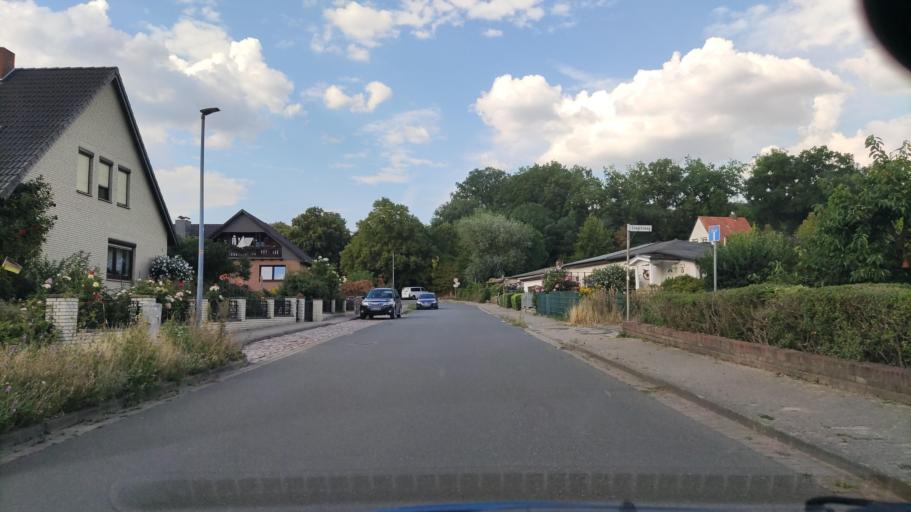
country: DE
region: Lower Saxony
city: Hitzacker
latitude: 53.1514
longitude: 11.0367
